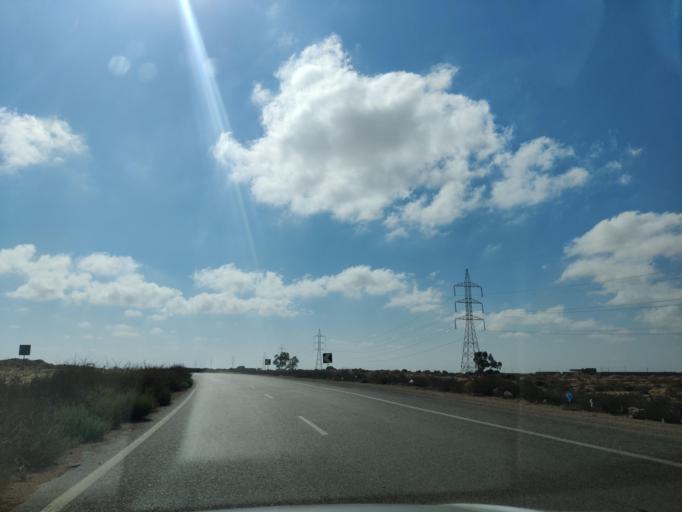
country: EG
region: Muhafazat Matruh
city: Al `Alamayn
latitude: 31.0542
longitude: 28.2624
